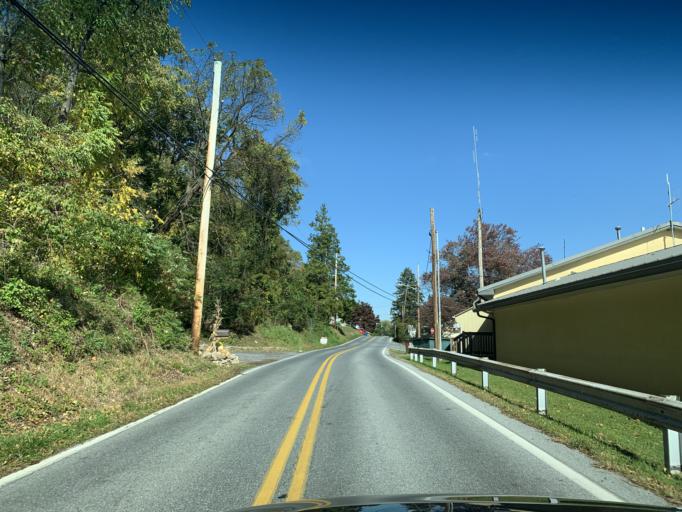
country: US
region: Pennsylvania
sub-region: Berks County
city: Reiffton
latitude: 40.3206
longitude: -75.8786
